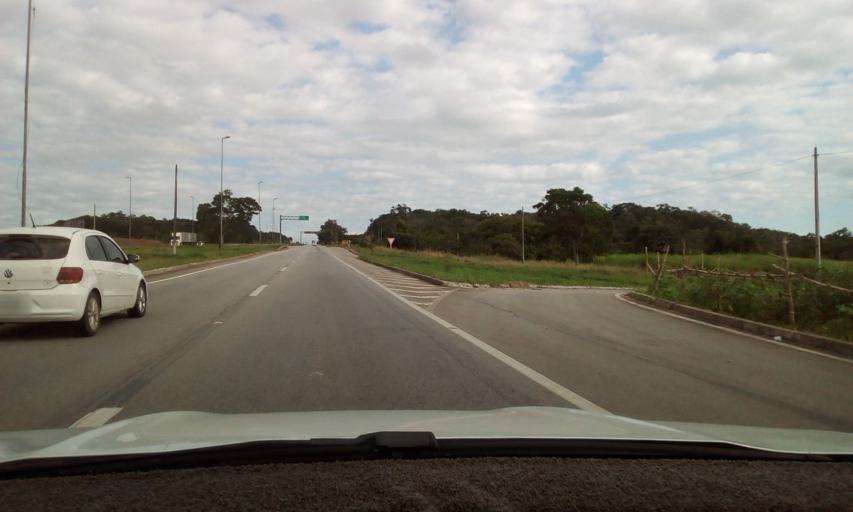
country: BR
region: Paraiba
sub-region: Mamanguape
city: Mamanguape
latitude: -6.8600
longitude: -35.1341
